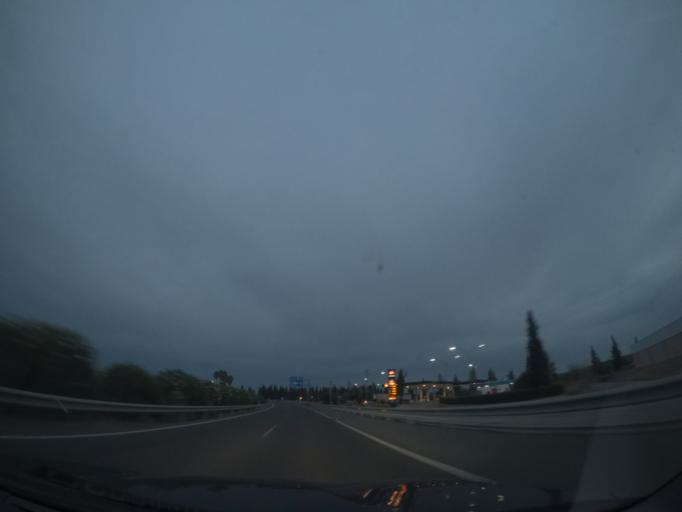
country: ES
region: Andalusia
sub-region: Provincia de Sevilla
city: El Arahal
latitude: 37.2547
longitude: -5.5634
